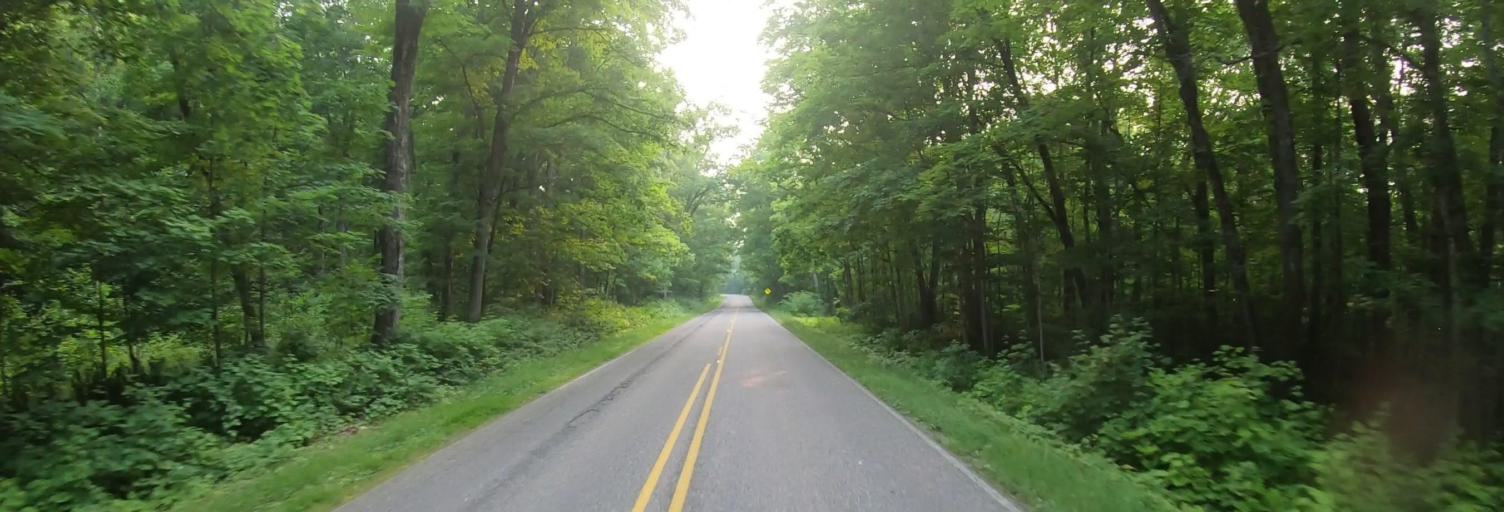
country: US
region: Michigan
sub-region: Chippewa County
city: Sault Ste. Marie
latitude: 46.4774
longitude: -84.6986
